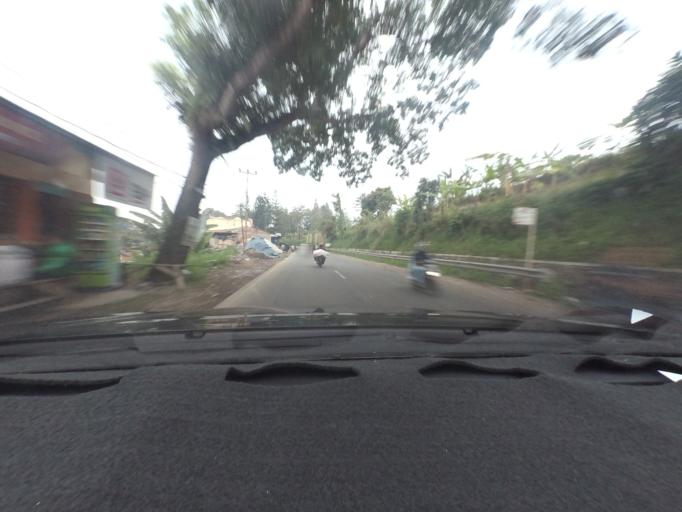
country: ID
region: West Java
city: Cicurug
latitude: -6.8039
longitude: 106.7730
